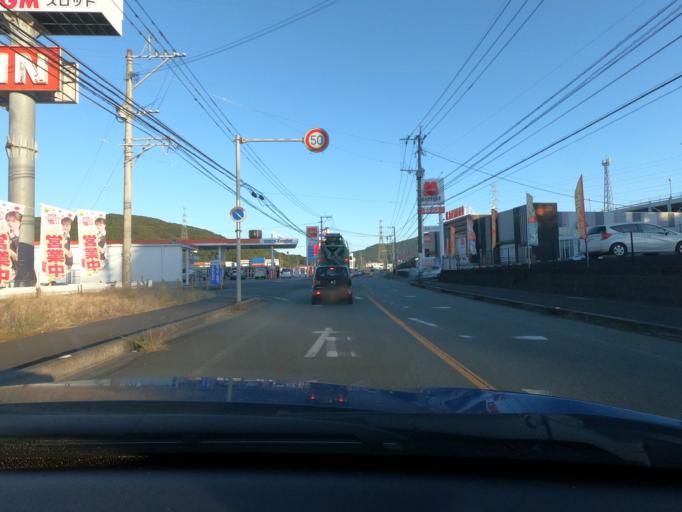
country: JP
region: Kagoshima
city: Satsumasendai
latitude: 31.8089
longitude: 130.3357
